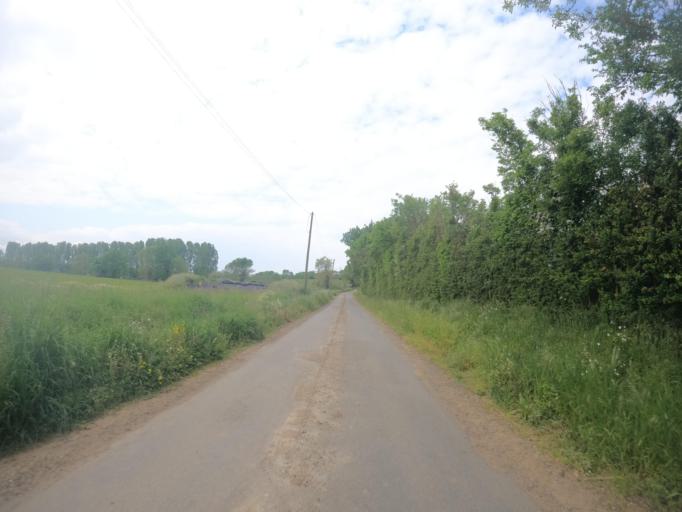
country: FR
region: Poitou-Charentes
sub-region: Departement des Deux-Sevres
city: Saint-Varent
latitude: 46.8739
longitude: -0.2786
